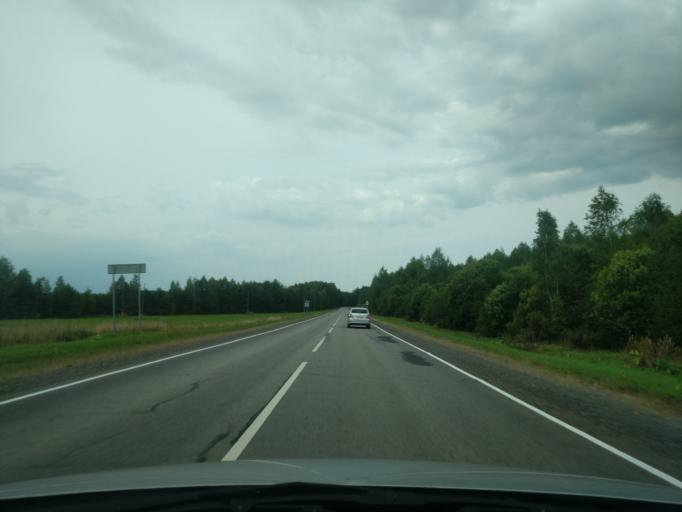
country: RU
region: Kirov
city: Svecha
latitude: 58.2722
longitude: 47.7363
